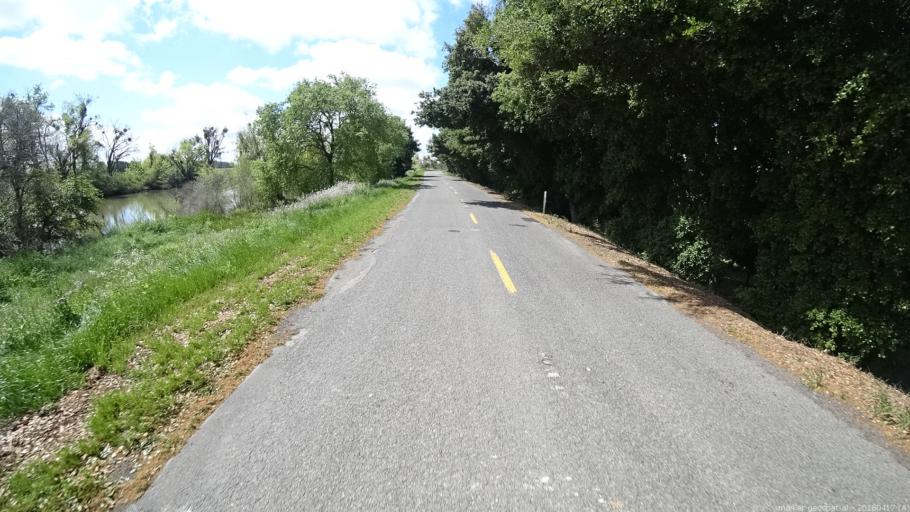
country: US
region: California
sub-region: Sacramento County
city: Walnut Grove
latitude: 38.2306
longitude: -121.5236
